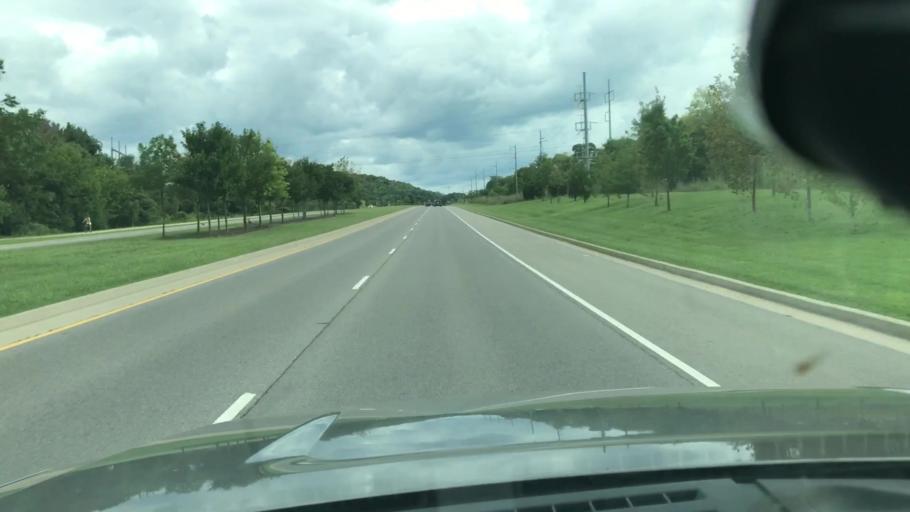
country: US
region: Tennessee
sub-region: Williamson County
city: Franklin
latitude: 35.9233
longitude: -86.8432
